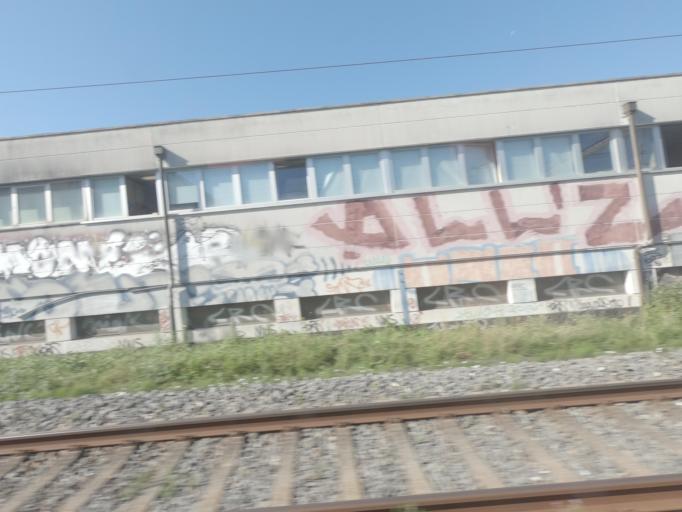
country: CH
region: Vaud
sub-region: Ouest Lausannois District
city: Bussigny
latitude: 46.5458
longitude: 6.5557
